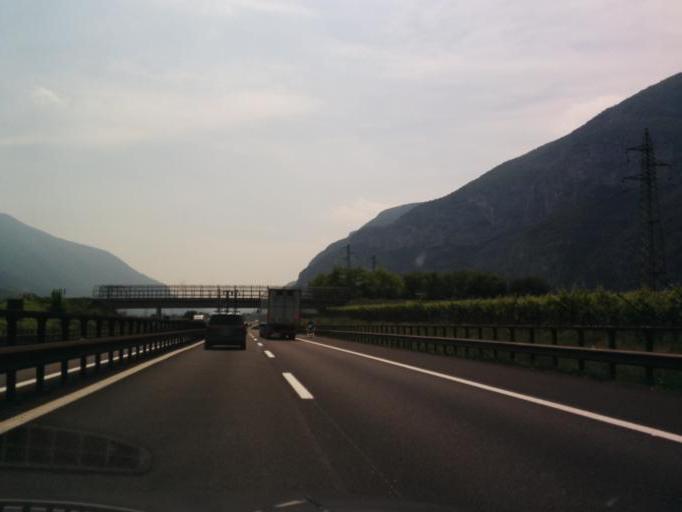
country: IT
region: Veneto
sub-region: Provincia di Verona
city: Dolce
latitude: 45.6259
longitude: 10.8654
